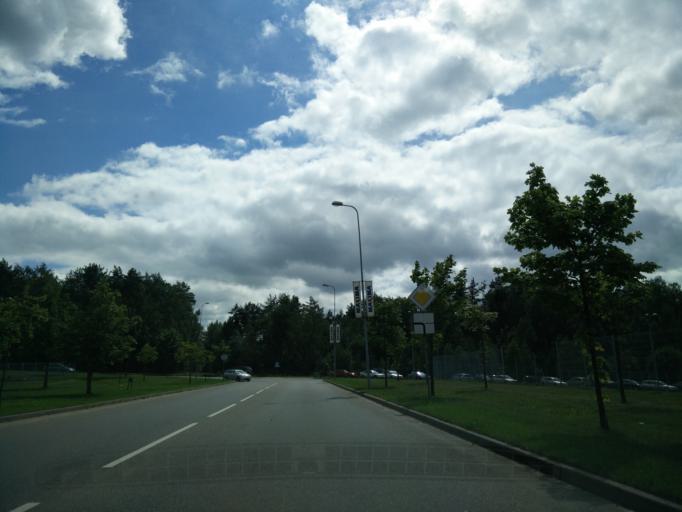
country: LT
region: Vilnius County
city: Pilaite
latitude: 54.6555
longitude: 25.1413
